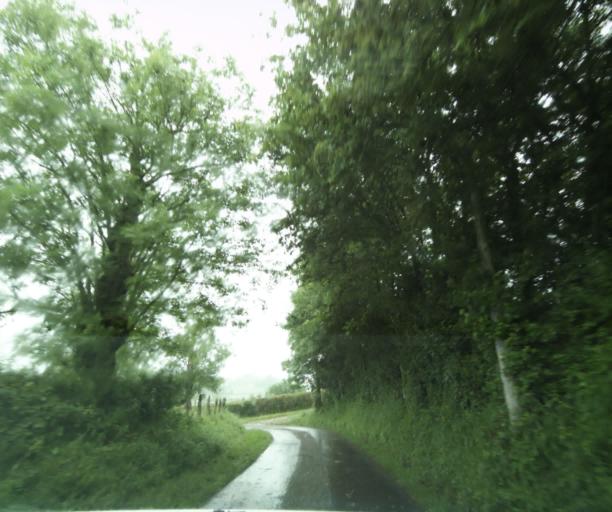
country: FR
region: Bourgogne
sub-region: Departement de Saone-et-Loire
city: Charolles
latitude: 46.4017
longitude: 4.2454
